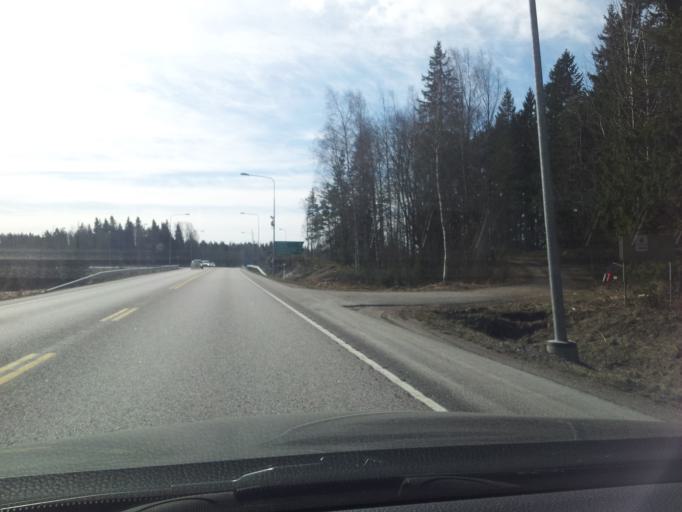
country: FI
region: Uusimaa
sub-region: Helsinki
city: Kirkkonummi
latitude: 60.1401
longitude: 24.5348
